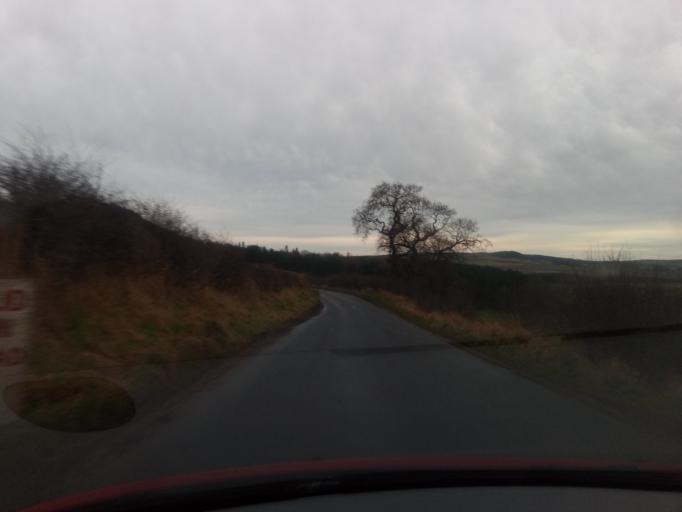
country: GB
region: England
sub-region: Northumberland
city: Whittingham
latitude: 55.4818
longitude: -1.8864
